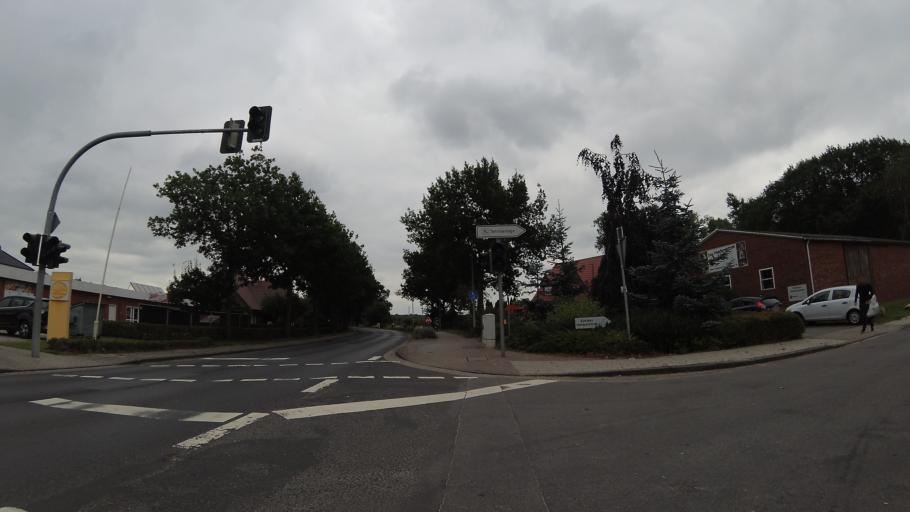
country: DE
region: Lower Saxony
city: Niederlangen
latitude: 52.8568
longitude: 7.2862
